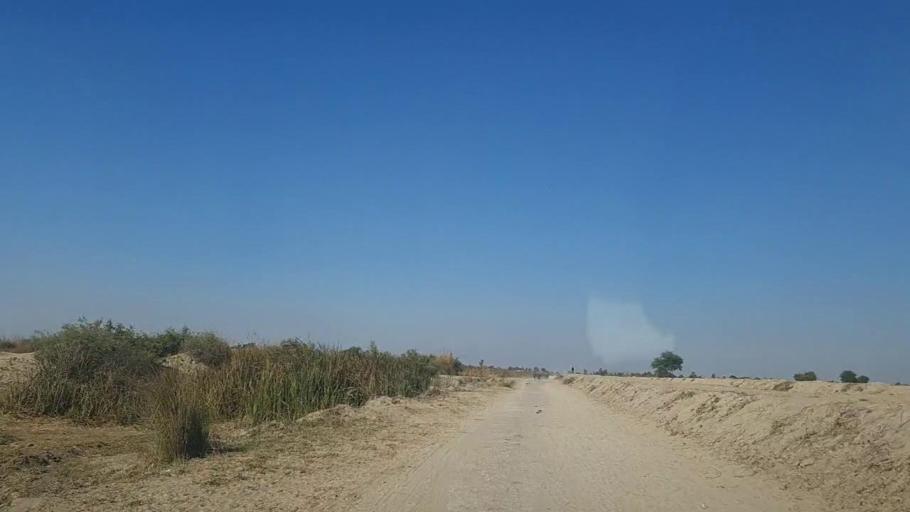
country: PK
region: Sindh
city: Sanghar
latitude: 26.2105
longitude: 68.9294
